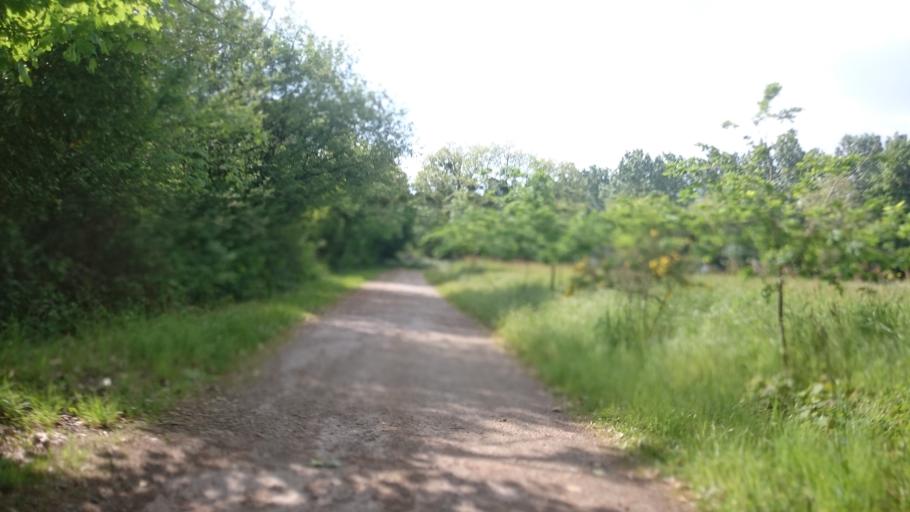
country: FR
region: Pays de la Loire
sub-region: Departement de la Loire-Atlantique
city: La Montagne
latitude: 47.1988
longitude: -1.6895
